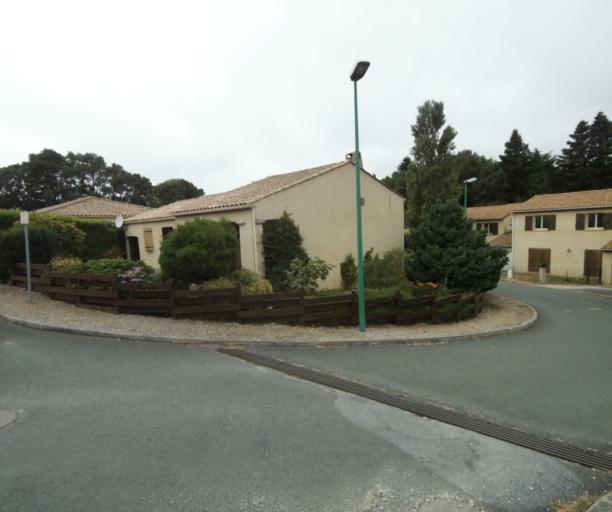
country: FR
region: Midi-Pyrenees
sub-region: Departement du Tarn
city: Soreze
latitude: 43.4088
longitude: 2.0786
